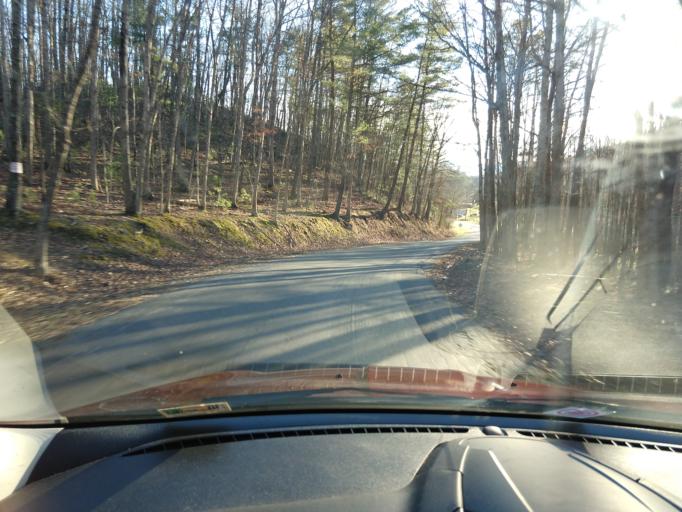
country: US
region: Virginia
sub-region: Alleghany County
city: Clifton Forge
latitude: 37.8440
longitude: -79.8476
